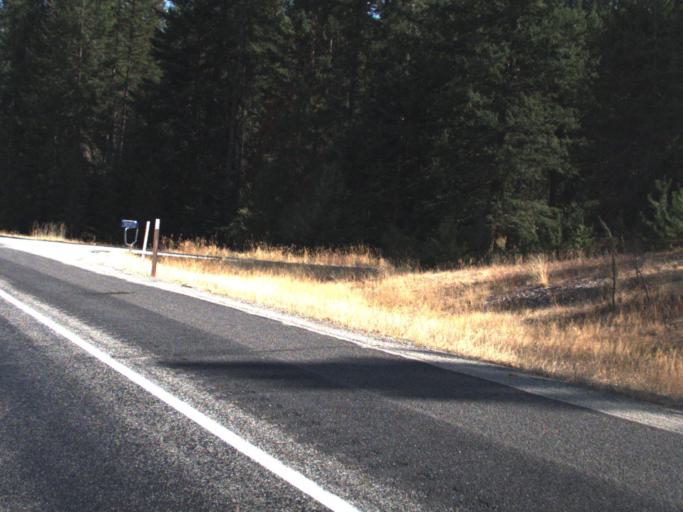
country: US
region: Washington
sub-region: Spokane County
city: Deer Park
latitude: 48.0967
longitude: -117.2899
